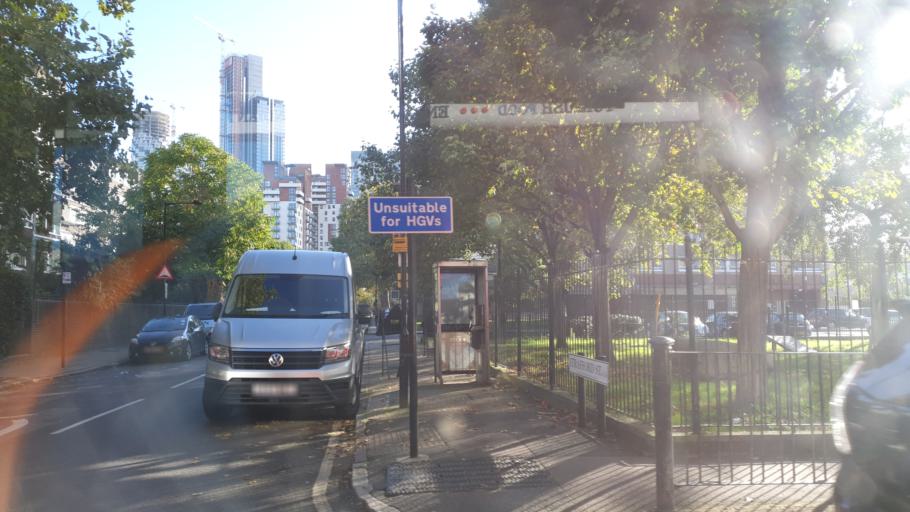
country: GB
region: England
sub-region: Greater London
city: Poplar
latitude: 51.4999
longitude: -0.0258
